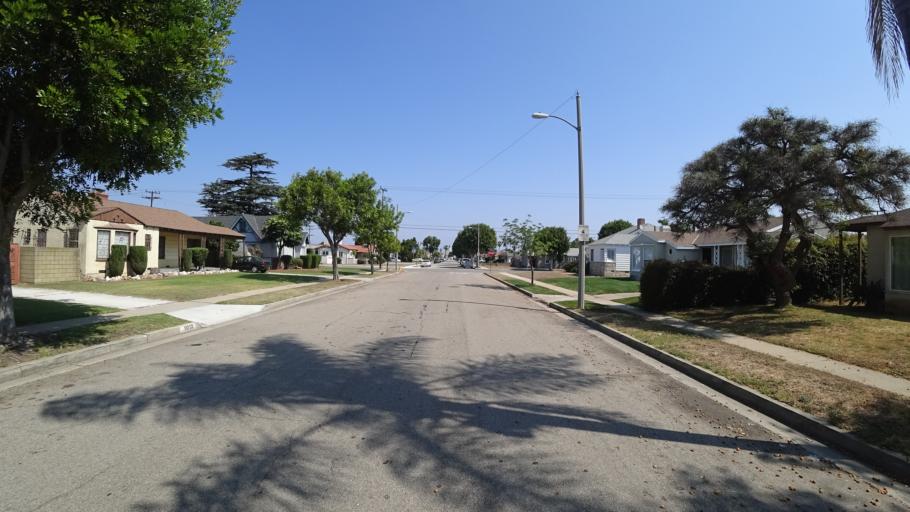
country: US
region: California
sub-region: Los Angeles County
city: Westmont
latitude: 33.9558
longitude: -118.3188
